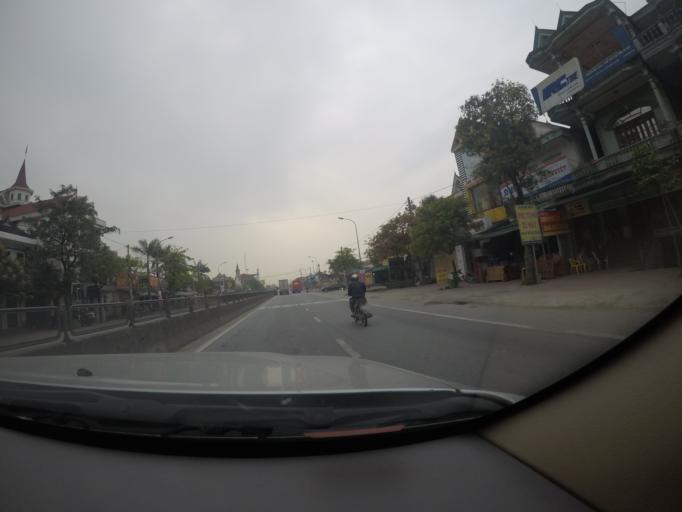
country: VN
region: Ha Tinh
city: Cam Xuyen
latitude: 18.2523
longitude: 105.9974
